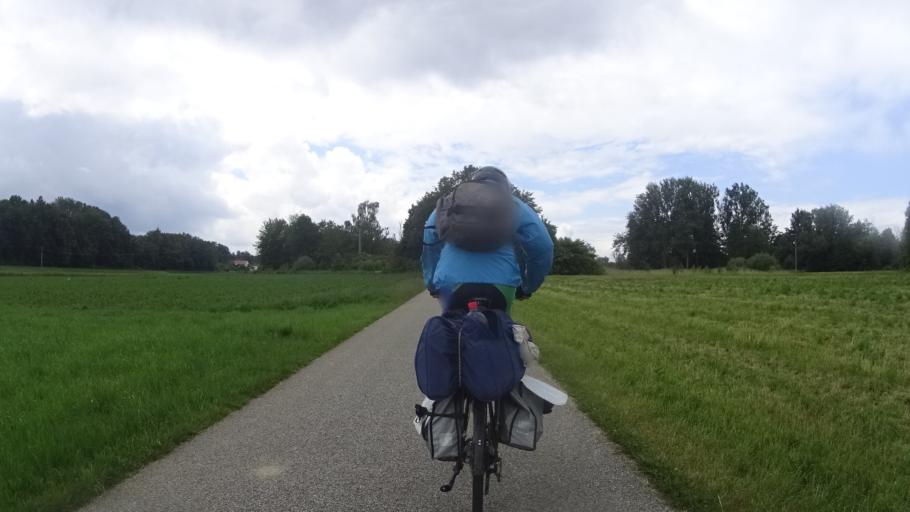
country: DE
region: Bavaria
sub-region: Lower Bavaria
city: Eggenfelden
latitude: 48.4042
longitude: 12.7851
